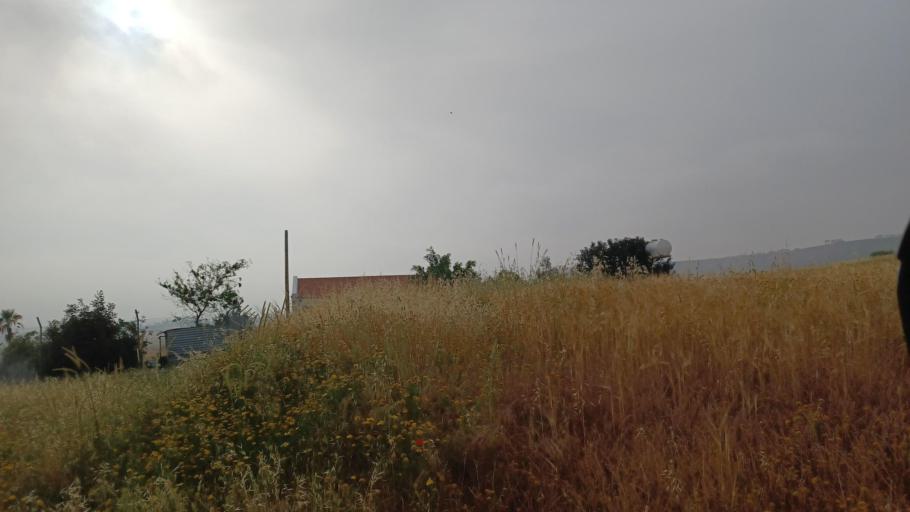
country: CY
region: Lefkosia
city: Mammari
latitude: 35.1805
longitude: 33.1886
